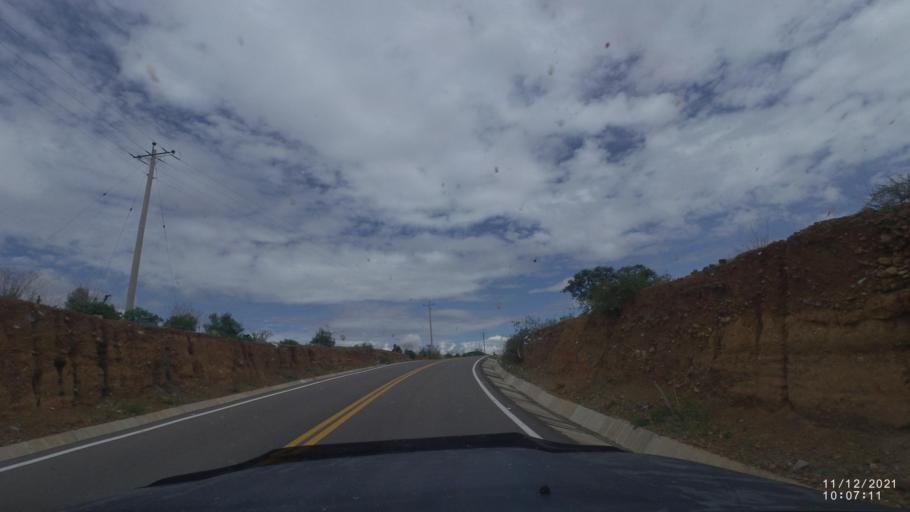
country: BO
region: Cochabamba
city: Cliza
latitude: -17.6823
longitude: -65.9540
